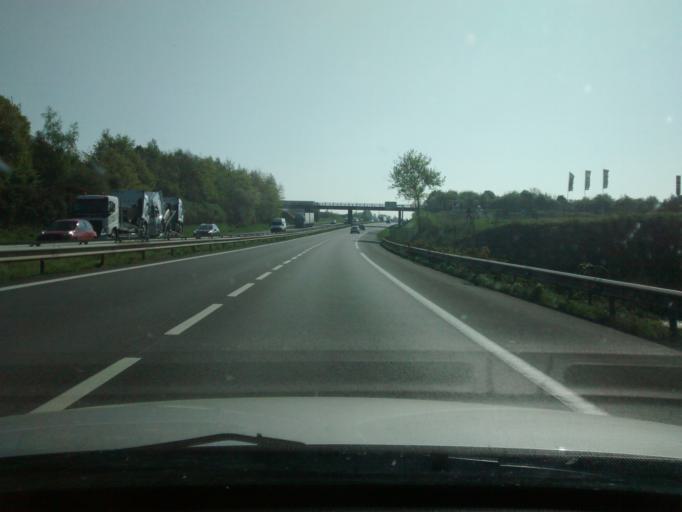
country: FR
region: Brittany
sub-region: Departement d'Ille-et-Vilaine
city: Brece
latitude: 48.1039
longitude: -1.4682
